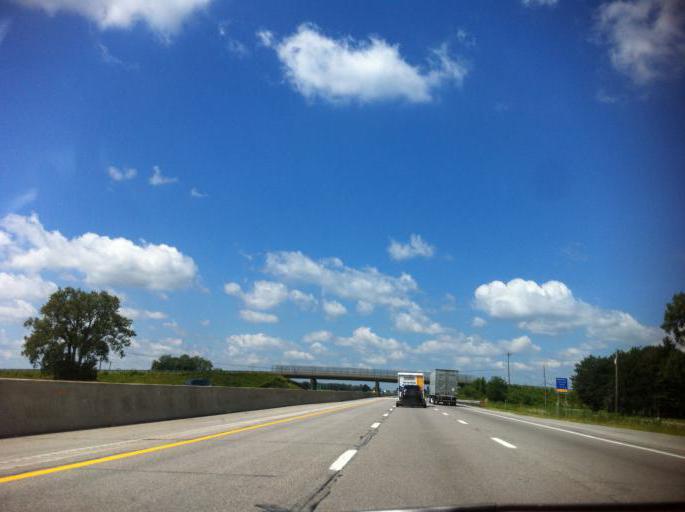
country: US
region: Ohio
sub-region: Sandusky County
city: Stony Prairie
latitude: 41.4293
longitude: -83.1989
